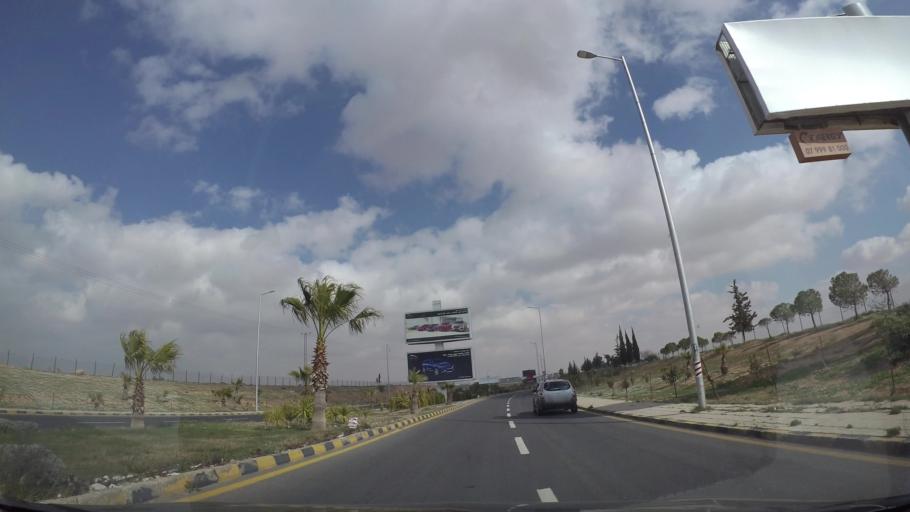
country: JO
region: Amman
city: Al Jizah
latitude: 31.7227
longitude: 35.9510
